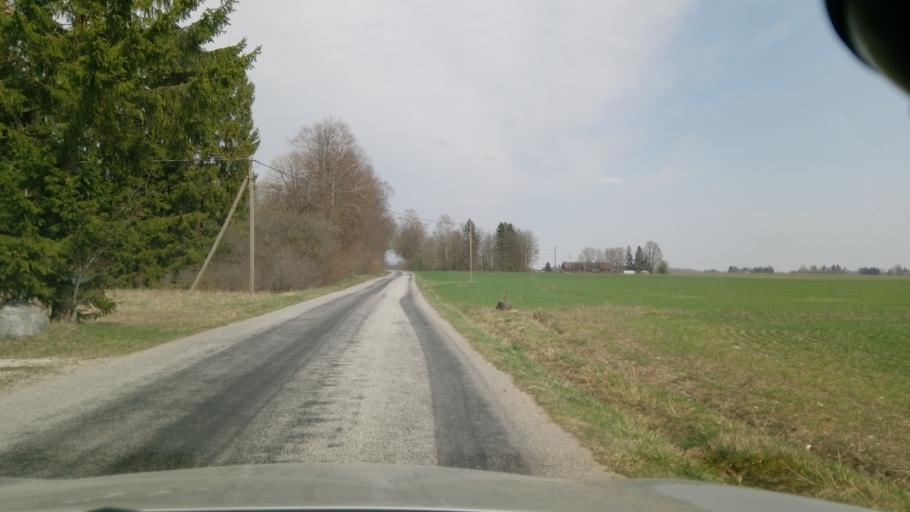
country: EE
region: Viljandimaa
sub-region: Vohma linn
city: Vohma
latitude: 58.6711
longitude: 25.5618
